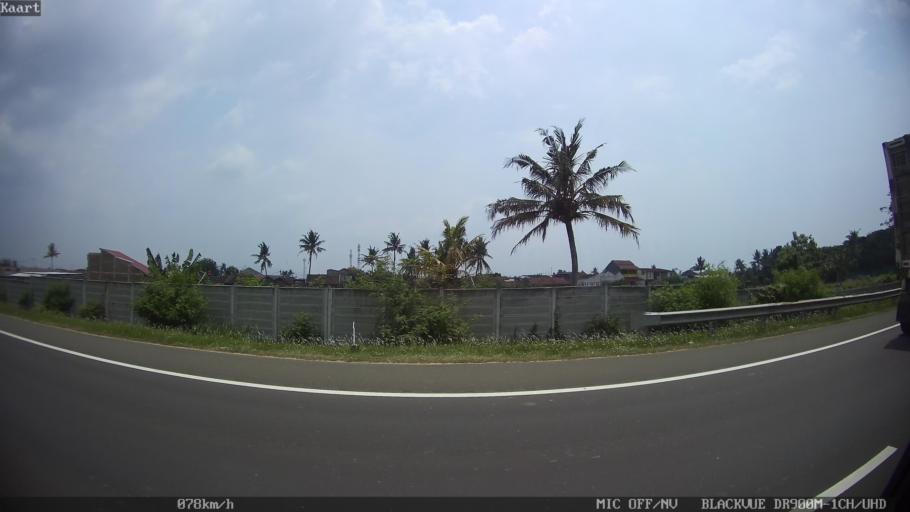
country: ID
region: Banten
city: Bojonegara
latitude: -6.0065
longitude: 106.0677
